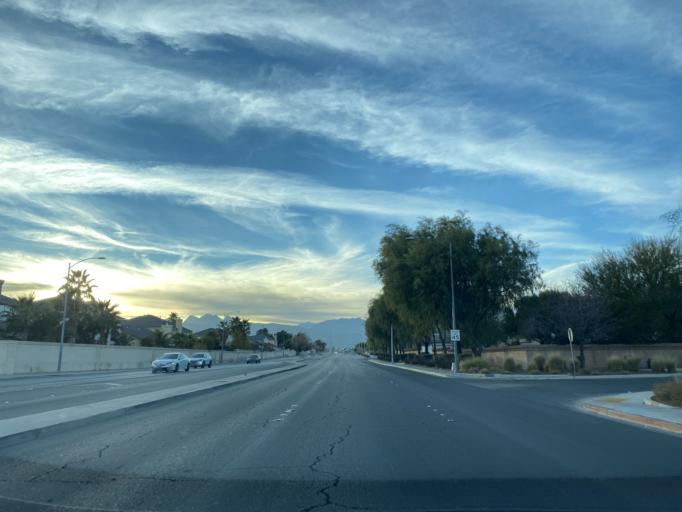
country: US
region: Nevada
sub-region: Clark County
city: Las Vegas
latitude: 36.2633
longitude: -115.2432
